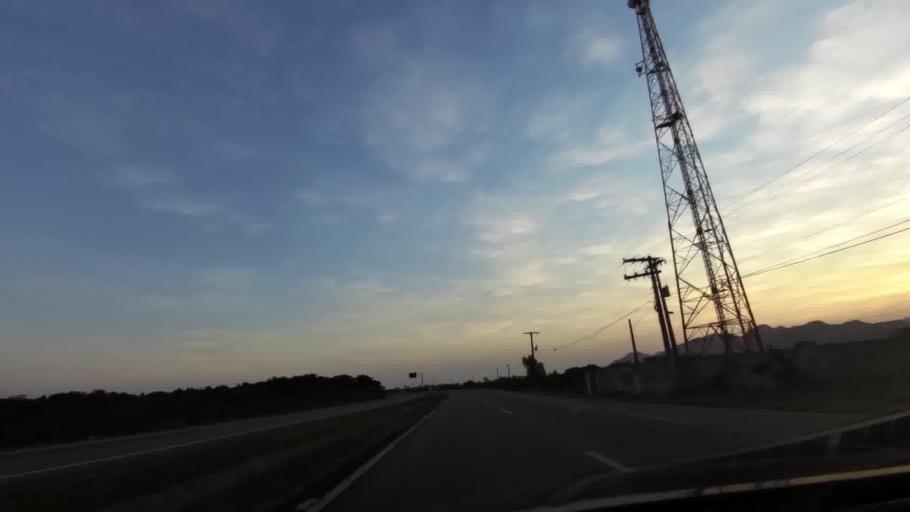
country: BR
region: Espirito Santo
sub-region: Guarapari
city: Guarapari
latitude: -20.5846
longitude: -40.4218
